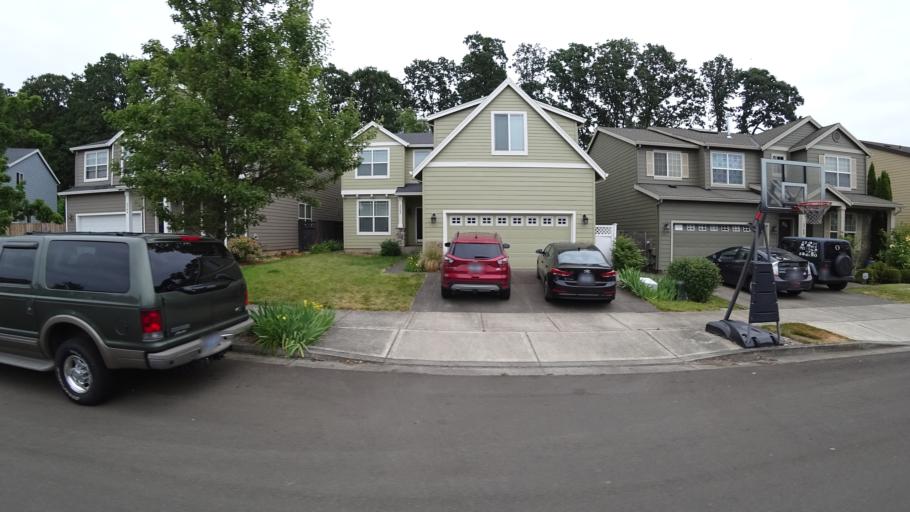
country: US
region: Oregon
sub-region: Washington County
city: Hillsboro
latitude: 45.4923
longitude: -122.9356
